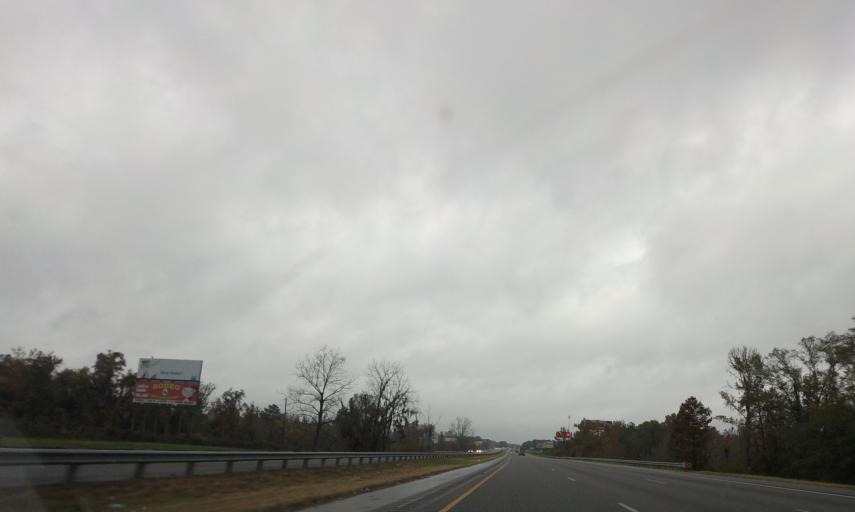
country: US
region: Georgia
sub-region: Echols County
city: Statenville
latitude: 30.6523
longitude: -83.1971
